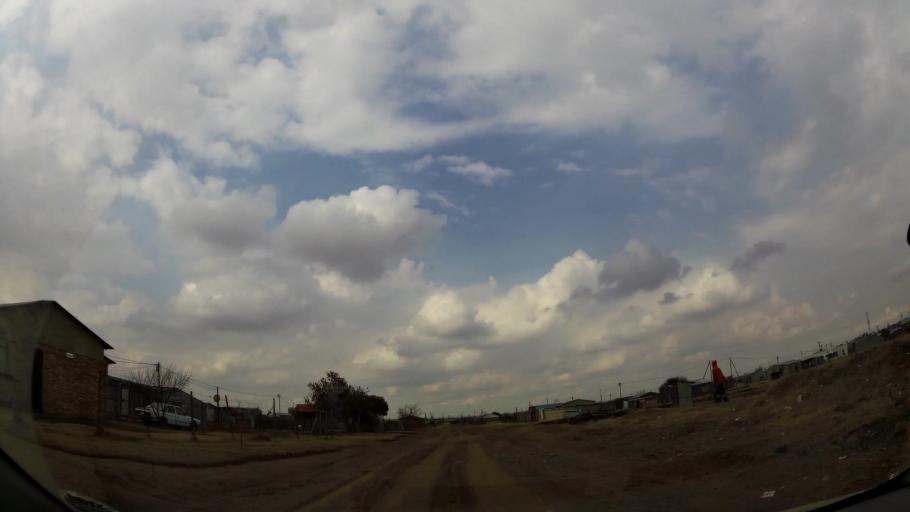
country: ZA
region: Orange Free State
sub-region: Fezile Dabi District Municipality
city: Sasolburg
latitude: -26.8633
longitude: 27.8937
